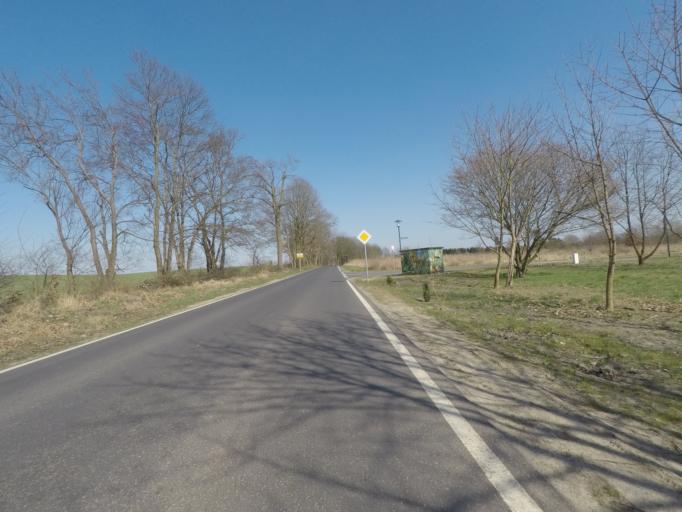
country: DE
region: Brandenburg
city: Britz
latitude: 52.8669
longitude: 13.7241
